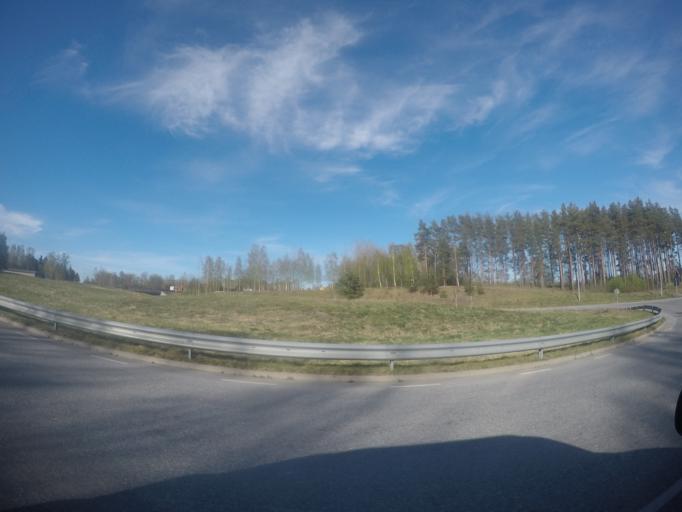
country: SE
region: OErebro
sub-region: Lindesbergs Kommun
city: Frovi
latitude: 59.3168
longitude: 15.4109
